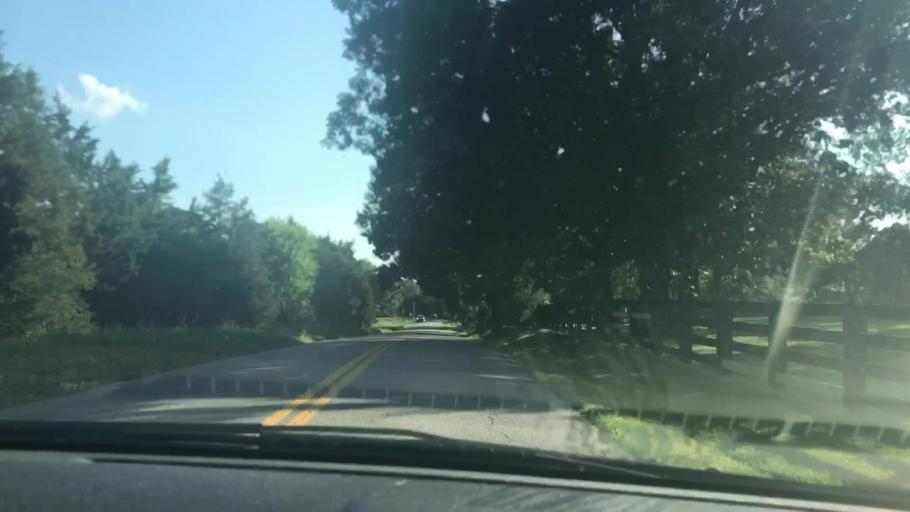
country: US
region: Virginia
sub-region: Henrico County
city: Short Pump
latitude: 37.6569
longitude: -77.7170
